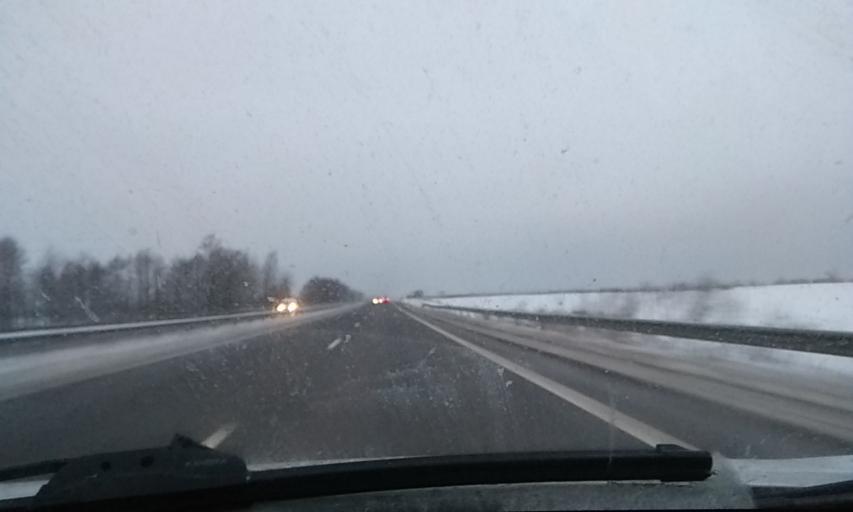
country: LT
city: Kaisiadorys
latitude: 54.8632
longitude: 24.2621
